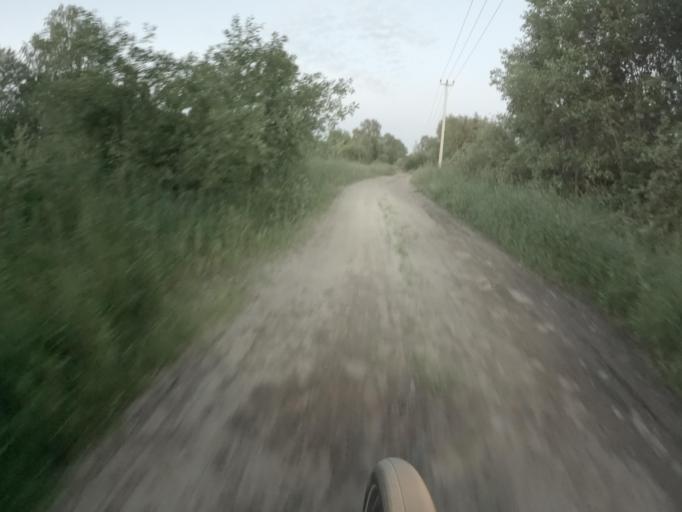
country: RU
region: Leningrad
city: Imeni Sverdlova
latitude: 59.7812
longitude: 30.6880
